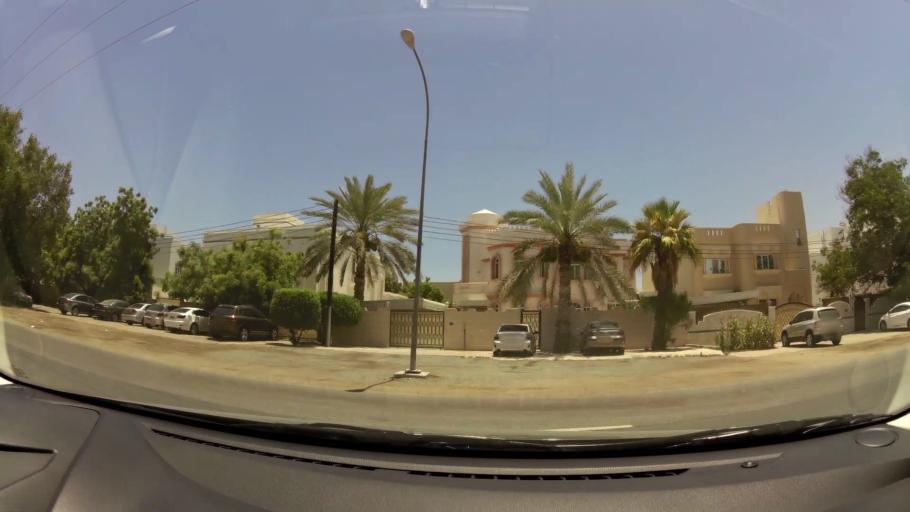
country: OM
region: Muhafazat Masqat
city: As Sib al Jadidah
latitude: 23.6375
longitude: 58.2375
